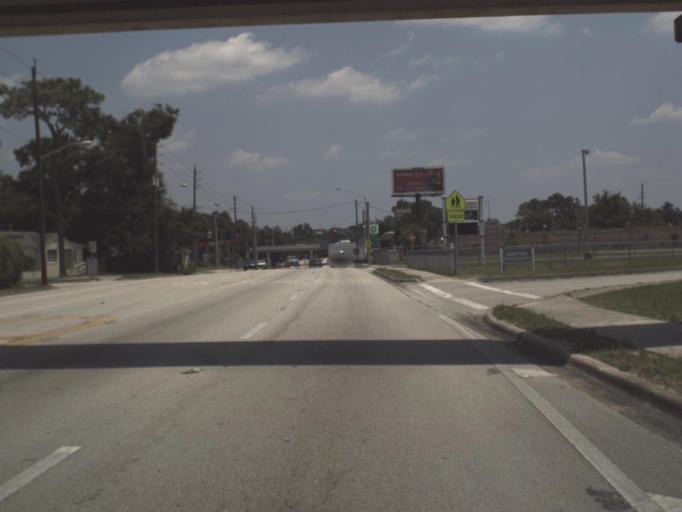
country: US
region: Florida
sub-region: Duval County
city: Jacksonville
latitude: 30.3923
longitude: -81.6715
